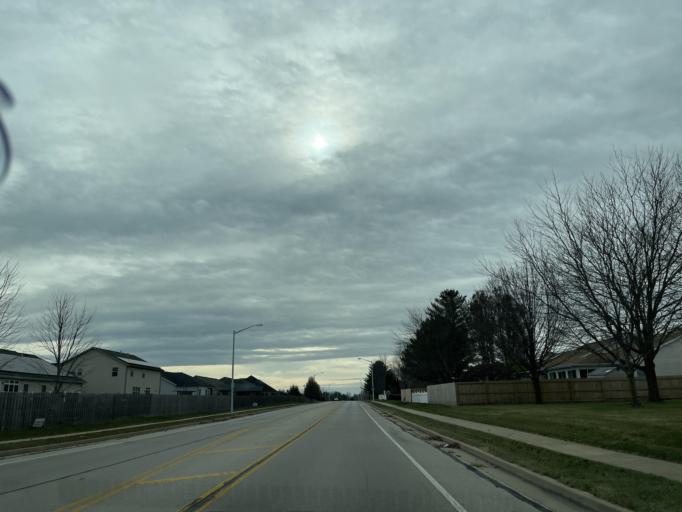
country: US
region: Illinois
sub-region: Sangamon County
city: Jerome
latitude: 39.7768
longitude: -89.7299
